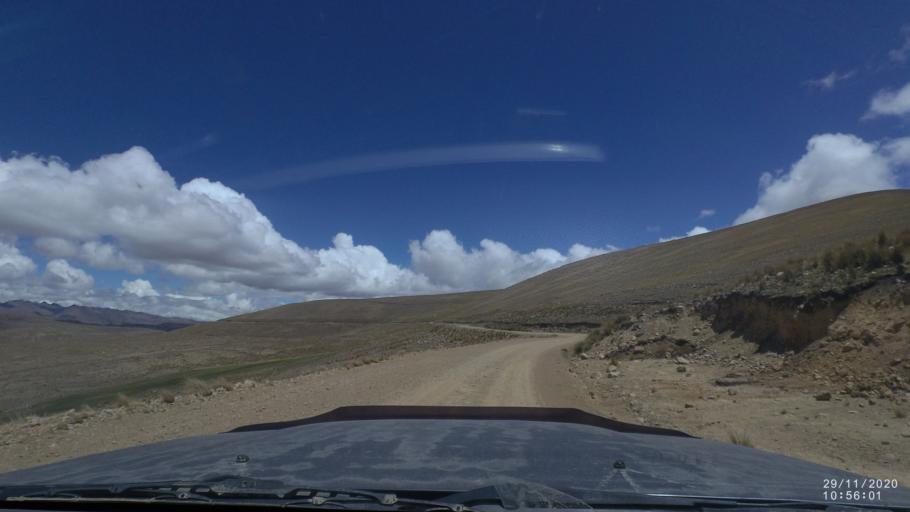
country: BO
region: Cochabamba
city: Cochabamba
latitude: -17.2223
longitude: -66.2240
